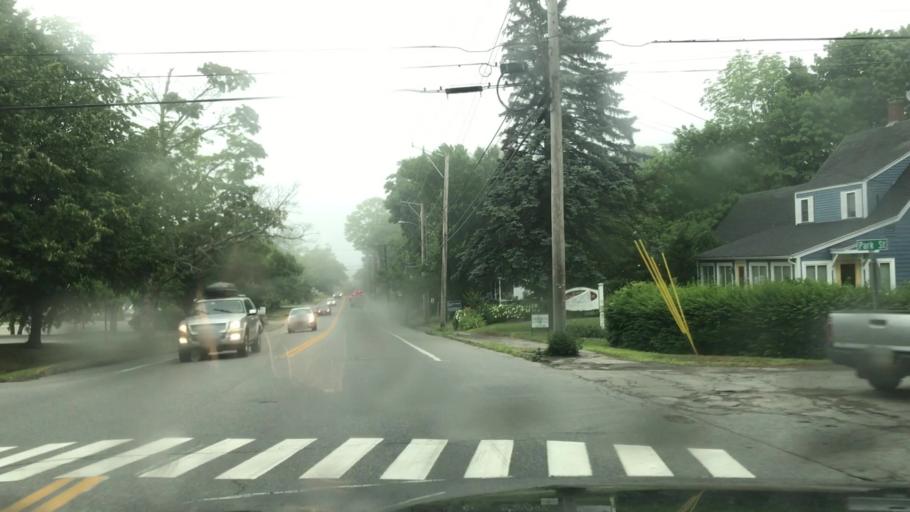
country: US
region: Maine
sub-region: Knox County
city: Camden
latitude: 44.2044
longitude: -69.0721
